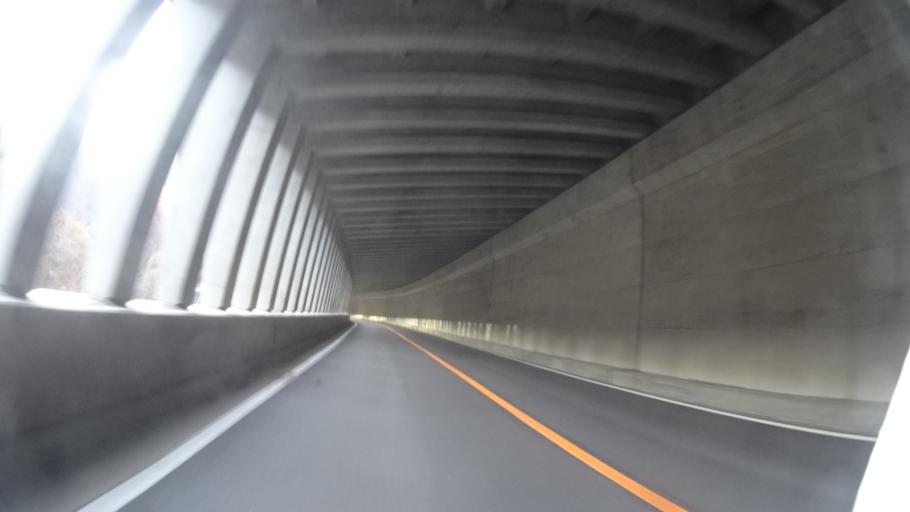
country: JP
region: Fukui
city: Ono
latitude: 35.9276
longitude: 136.6389
